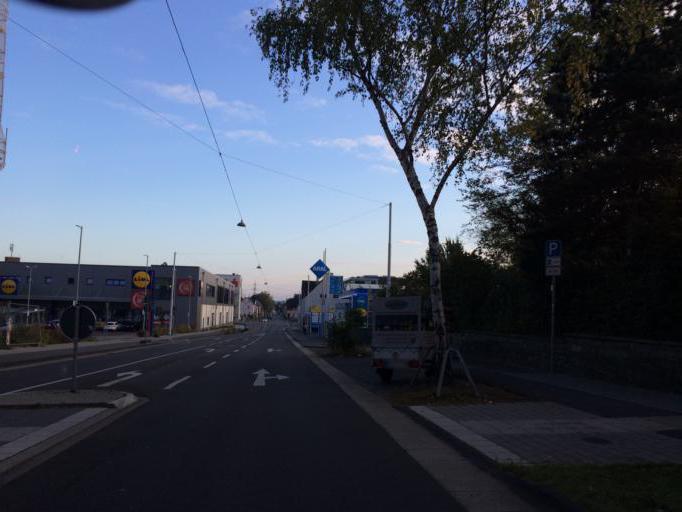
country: DE
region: North Rhine-Westphalia
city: Sankt Augustin
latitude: 50.7779
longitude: 7.1902
